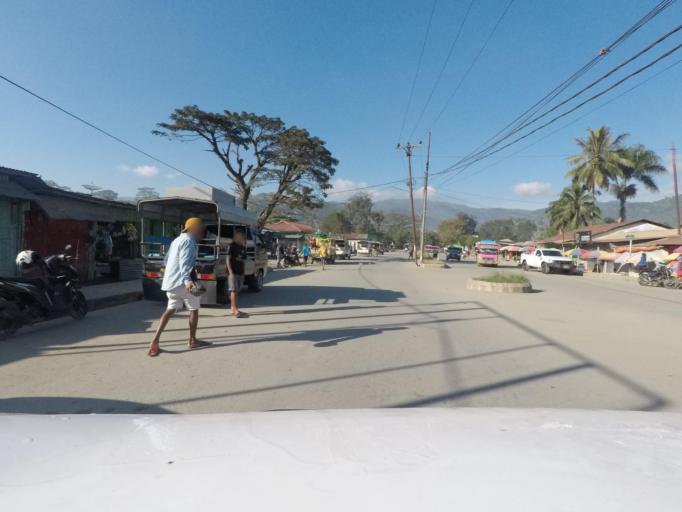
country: TL
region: Ermera
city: Gleno
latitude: -8.7230
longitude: 125.4362
